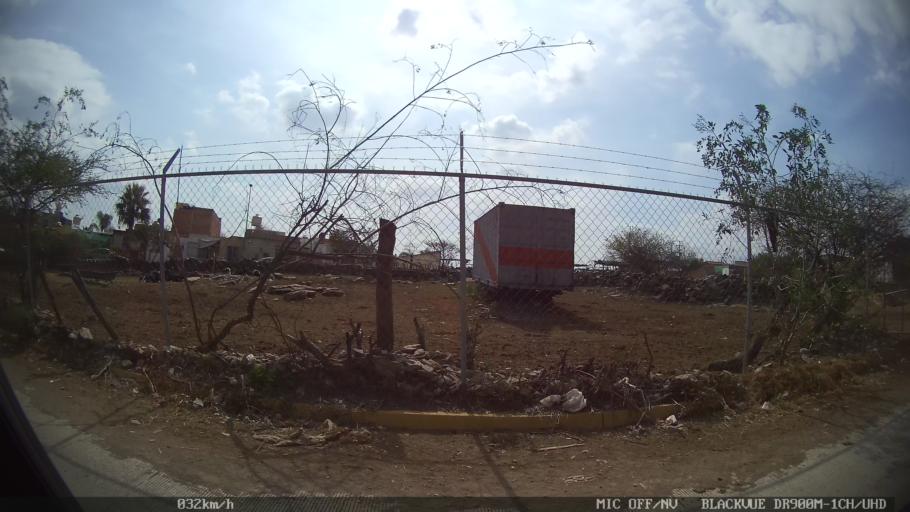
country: MX
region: Jalisco
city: Coyula
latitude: 20.6486
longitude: -103.2140
